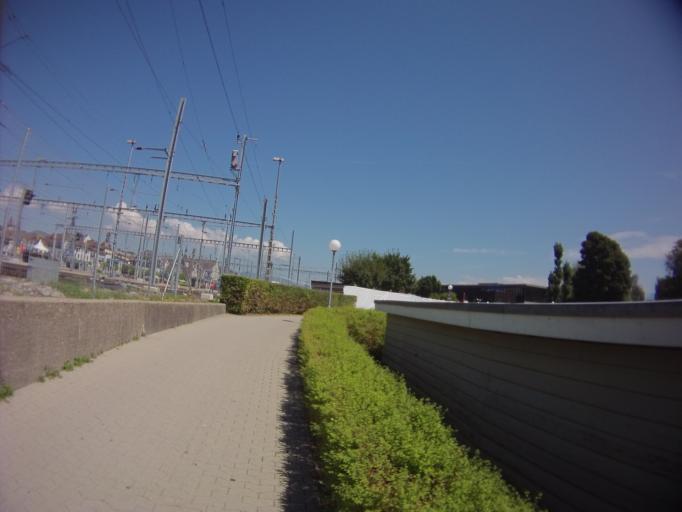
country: CH
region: Saint Gallen
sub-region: Wahlkreis See-Gaster
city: Rapperswil
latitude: 47.2240
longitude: 8.8143
